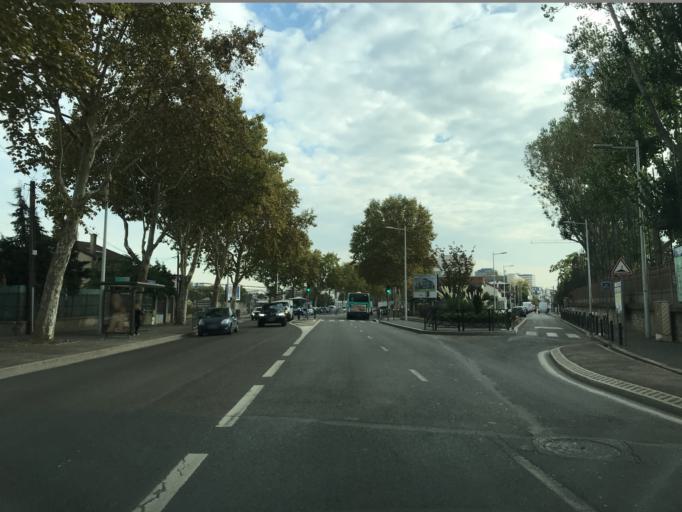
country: FR
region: Ile-de-France
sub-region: Departement des Hauts-de-Seine
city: La Defense
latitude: 48.9024
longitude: 2.2274
